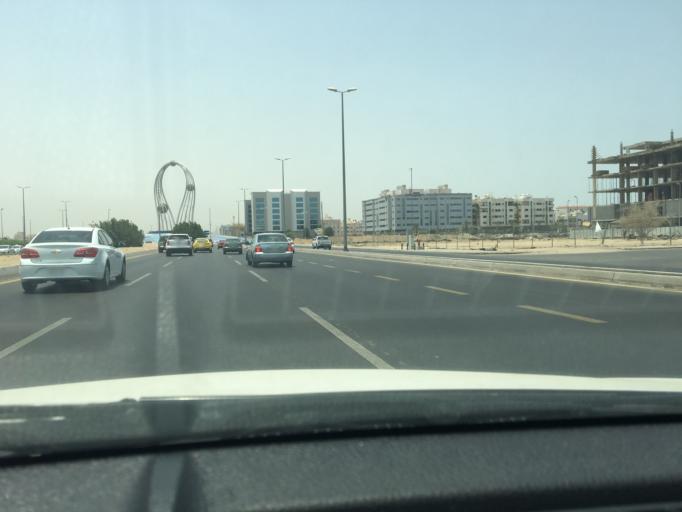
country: SA
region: Makkah
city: Jeddah
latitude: 21.5868
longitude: 39.1761
